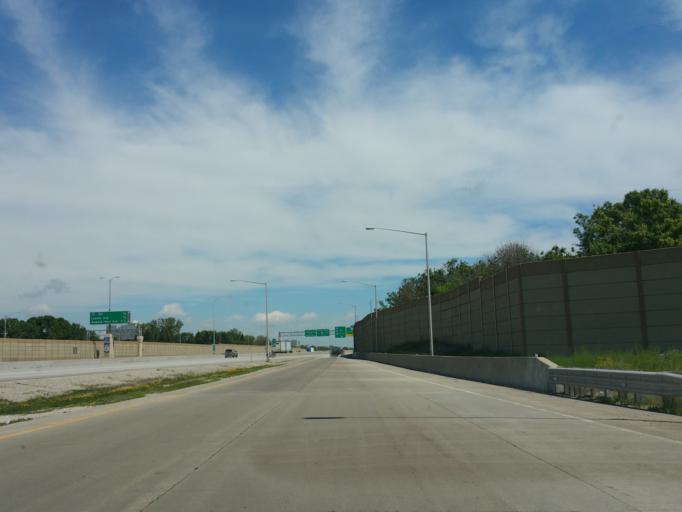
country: US
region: Wisconsin
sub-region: Milwaukee County
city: Greendale
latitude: 42.9321
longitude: -87.9347
